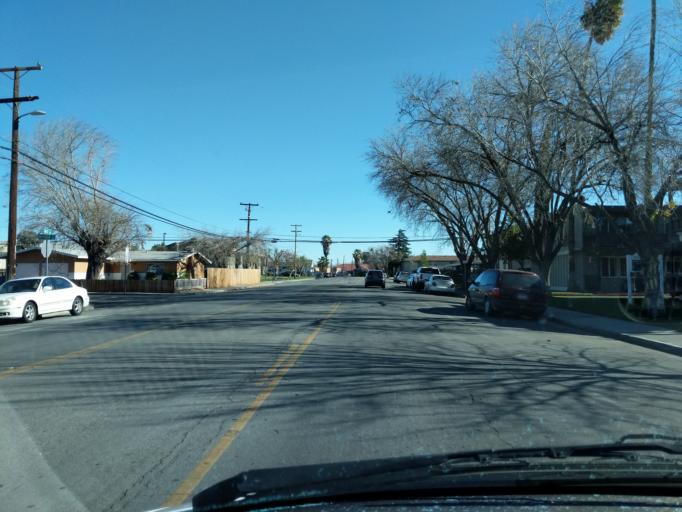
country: US
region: California
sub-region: Merced County
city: Los Banos
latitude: 37.0634
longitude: -120.8564
